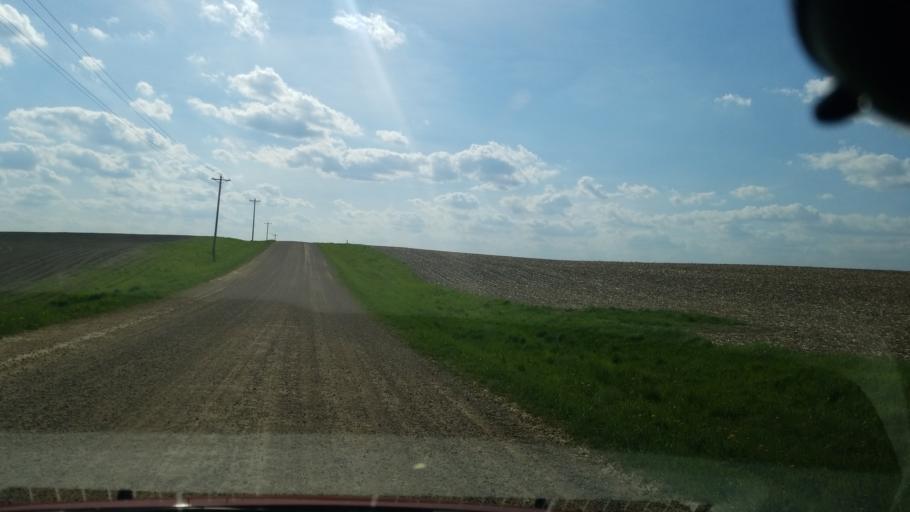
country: US
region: Iowa
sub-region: Jackson County
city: Maquoketa
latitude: 42.2150
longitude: -90.7190
